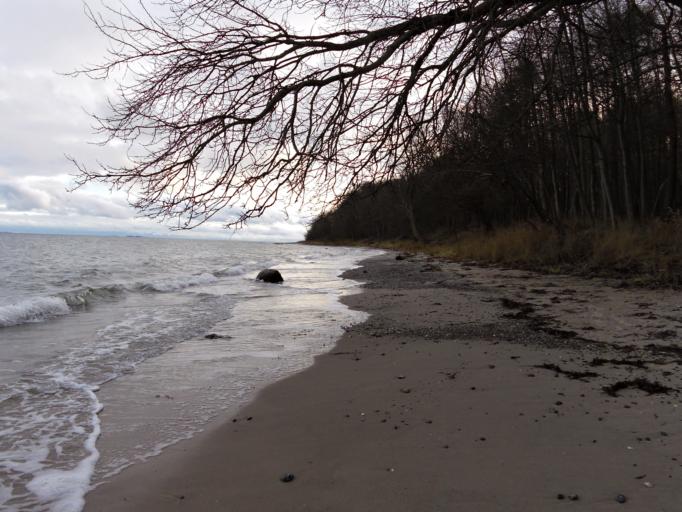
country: DK
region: Central Jutland
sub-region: Arhus Kommune
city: Beder
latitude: 56.0709
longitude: 10.2559
